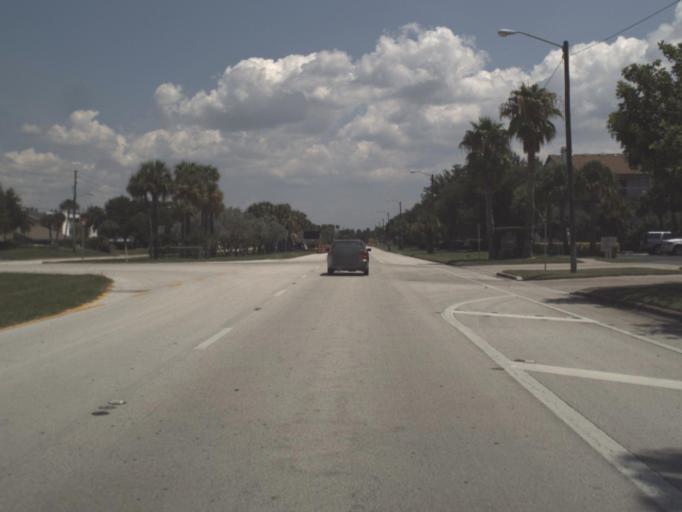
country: US
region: Florida
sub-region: Pinellas County
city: Tierra Verde
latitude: 27.6854
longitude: -82.7230
